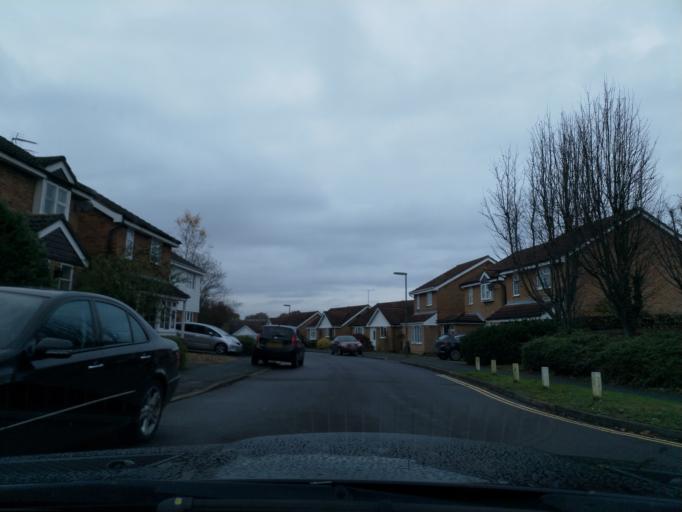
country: GB
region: England
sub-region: Surrey
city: Frimley
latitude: 51.3100
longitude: -0.7270
